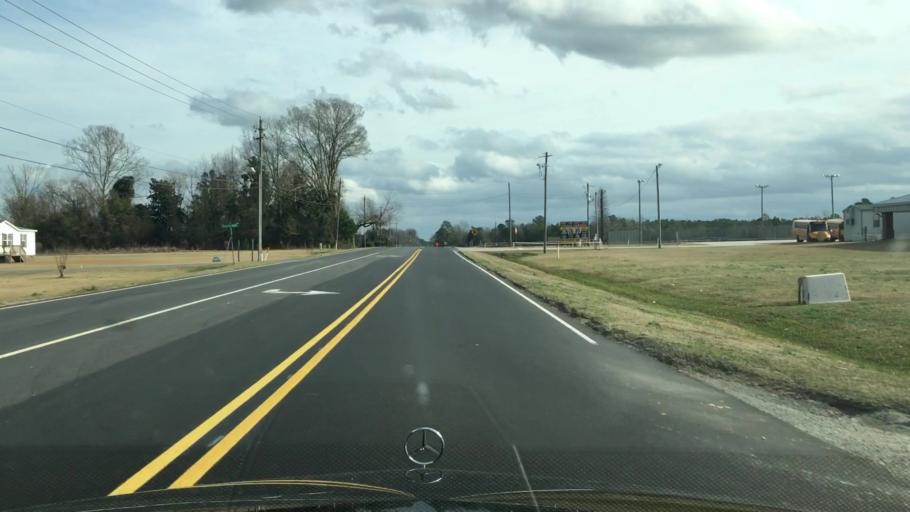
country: US
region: North Carolina
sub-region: Duplin County
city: Warsaw
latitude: 34.9851
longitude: -78.0422
